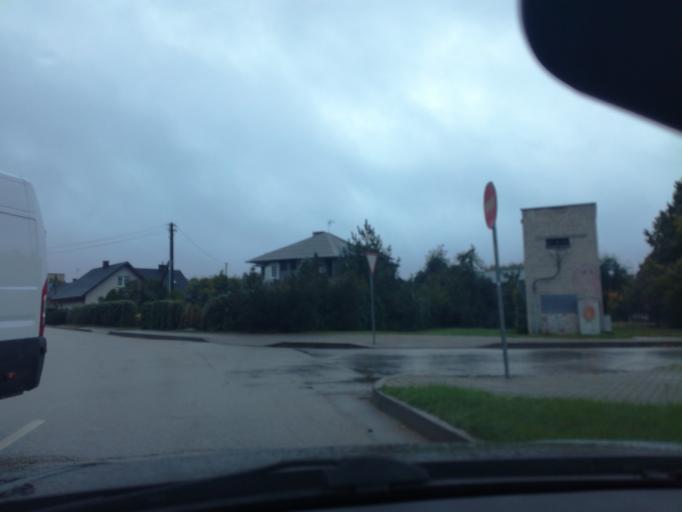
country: LT
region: Alytaus apskritis
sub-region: Alytus
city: Alytus
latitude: 54.4025
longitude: 24.0660
